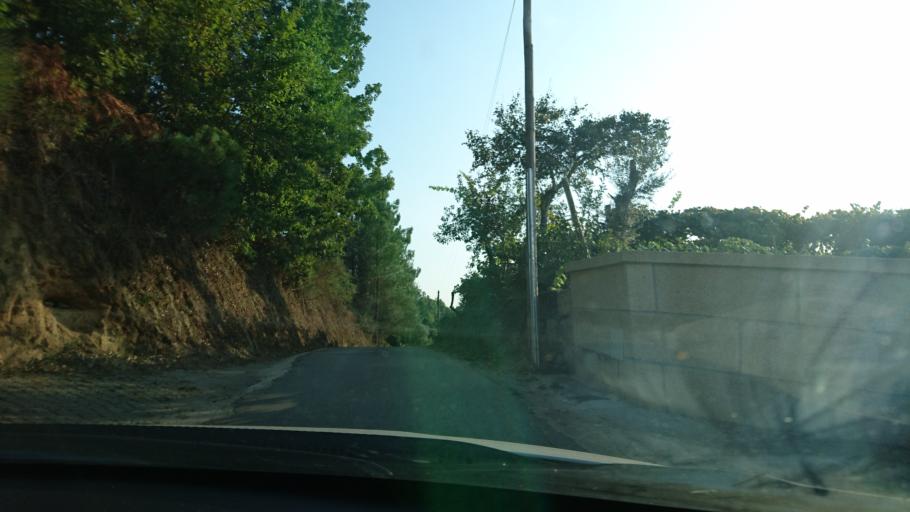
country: PT
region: Vila Real
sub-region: Mondim de Basto
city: Mondim de Basto
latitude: 41.4508
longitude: -7.9278
